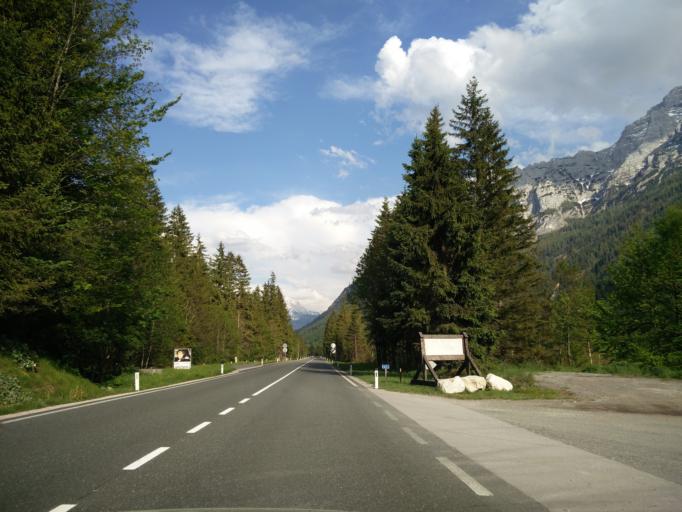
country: AT
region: Tyrol
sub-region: Politischer Bezirk Kitzbuhel
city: Waidring
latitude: 47.5870
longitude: 12.6119
